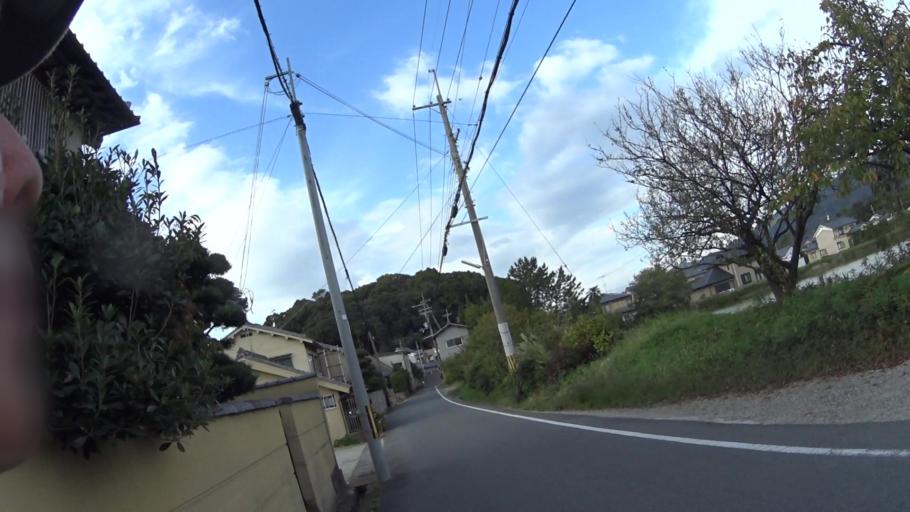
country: JP
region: Nara
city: Sakurai
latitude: 34.5369
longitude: 135.8417
